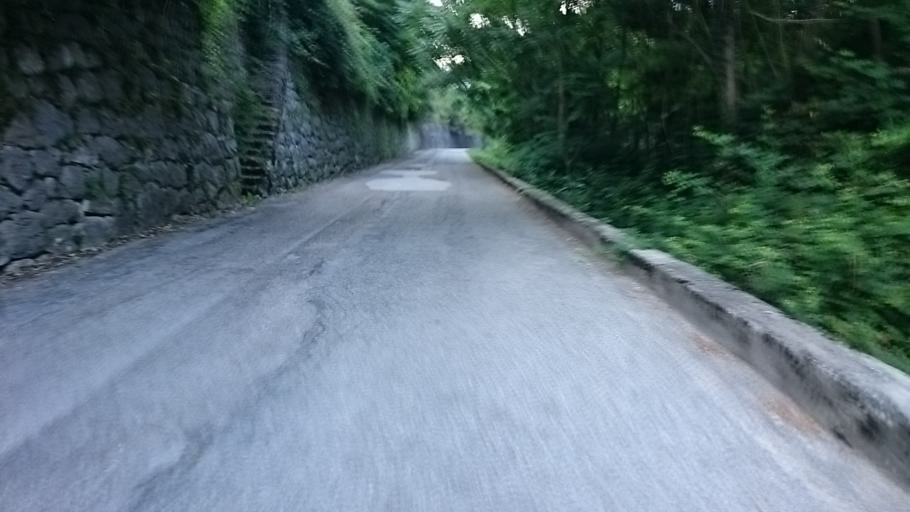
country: IT
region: Veneto
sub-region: Provincia di Vicenza
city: Cismon del Grappa
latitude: 45.9195
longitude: 11.7228
